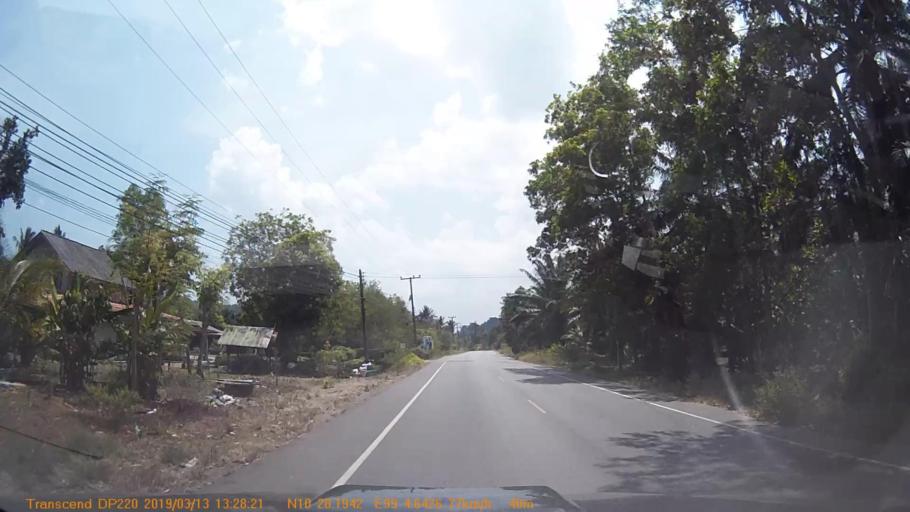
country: TH
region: Chumphon
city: Chumphon
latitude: 10.4744
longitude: 99.0782
